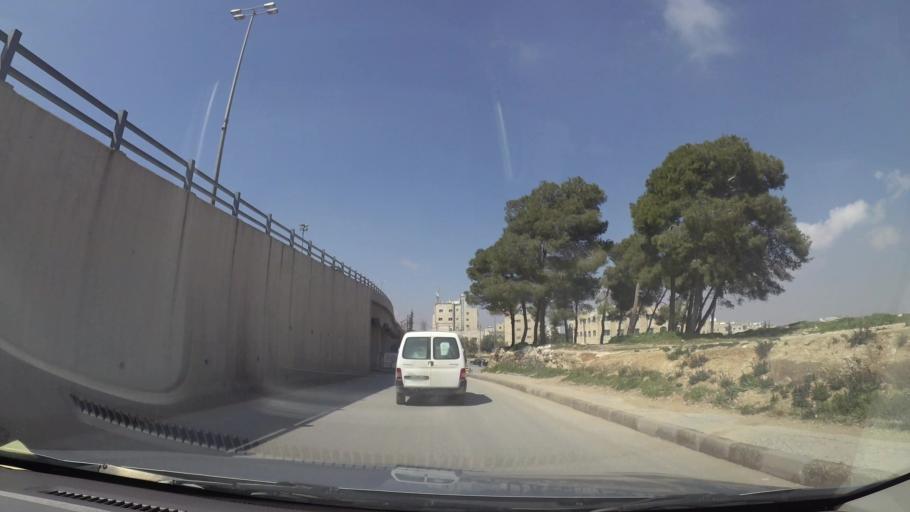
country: JO
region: Amman
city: Al Bunayyat ash Shamaliyah
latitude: 31.9200
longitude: 35.8954
